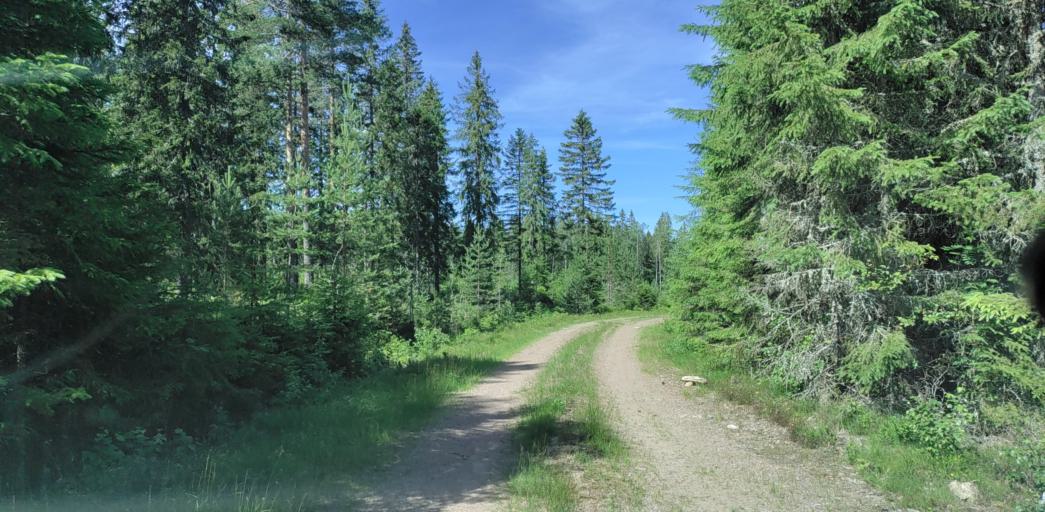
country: SE
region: Vaermland
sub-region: Hagfors Kommun
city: Ekshaerad
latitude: 60.0903
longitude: 13.3763
